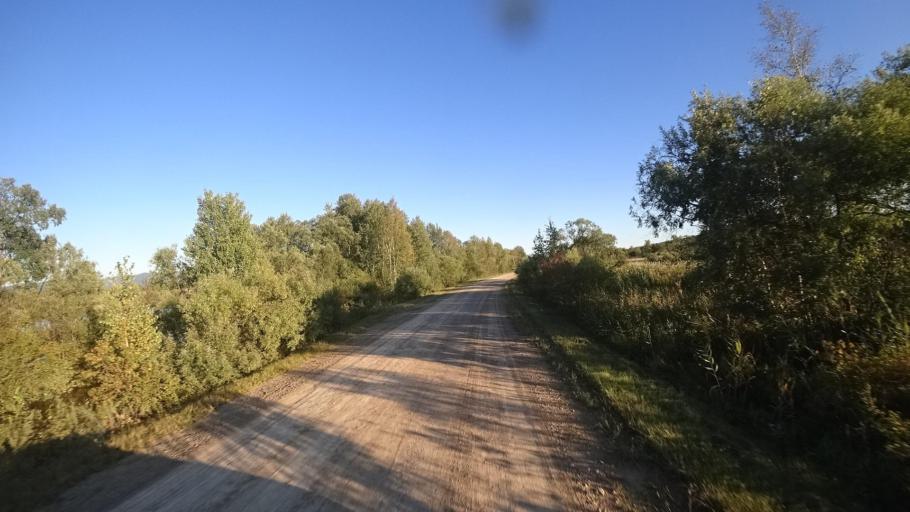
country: RU
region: Primorskiy
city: Kirovskiy
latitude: 44.7865
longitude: 133.6236
